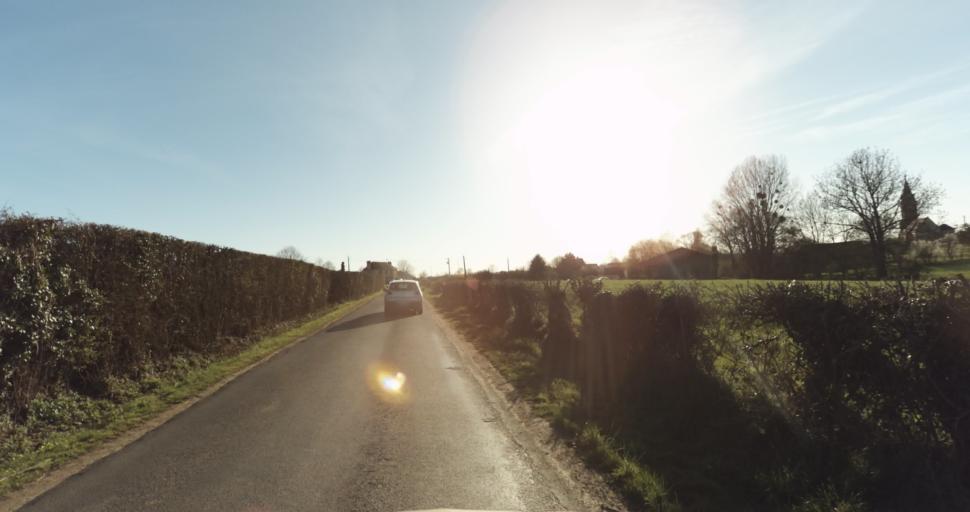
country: FR
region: Lower Normandy
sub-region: Departement de l'Orne
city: Trun
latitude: 48.9406
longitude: 0.0361
